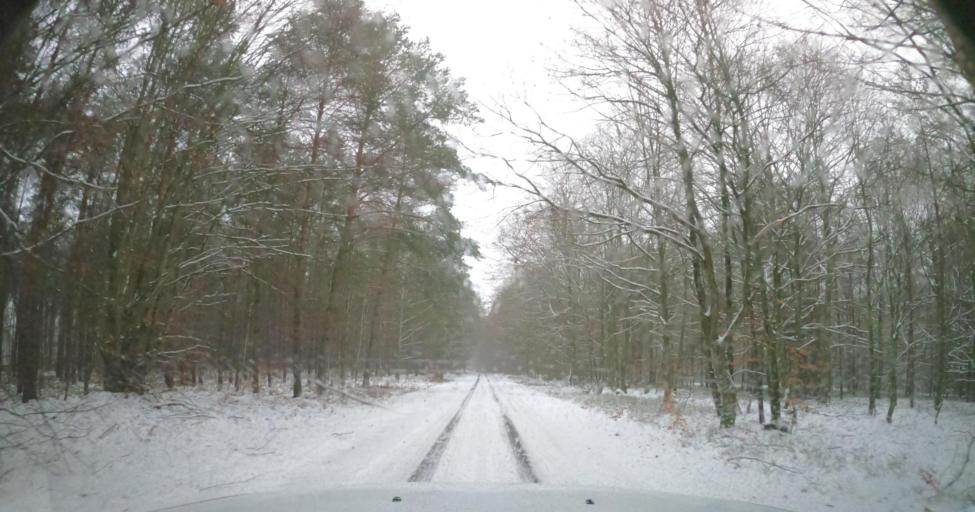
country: PL
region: West Pomeranian Voivodeship
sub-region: Powiat goleniowski
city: Przybiernow
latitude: 53.6622
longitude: 14.7674
